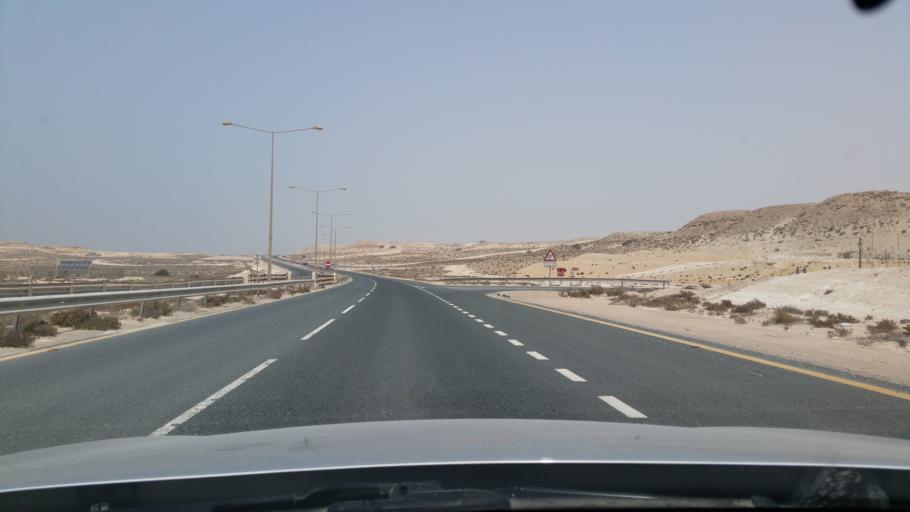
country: QA
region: Baladiyat ar Rayyan
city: Dukhan
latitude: 25.3450
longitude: 50.7830
